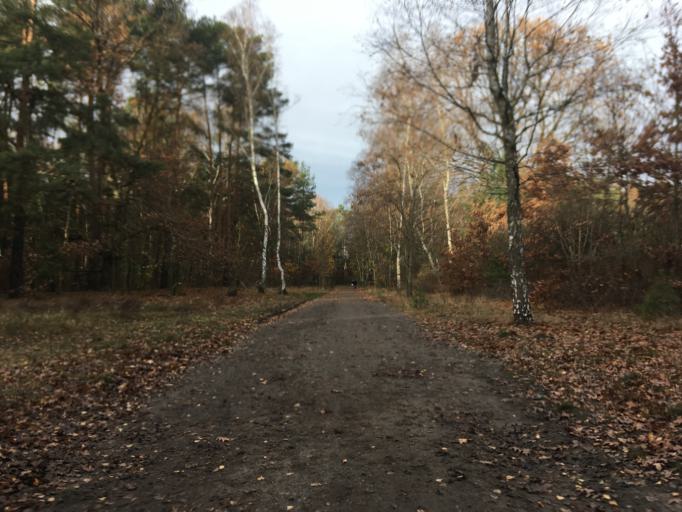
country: DE
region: Berlin
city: Adlershof
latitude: 52.4459
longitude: 13.5408
